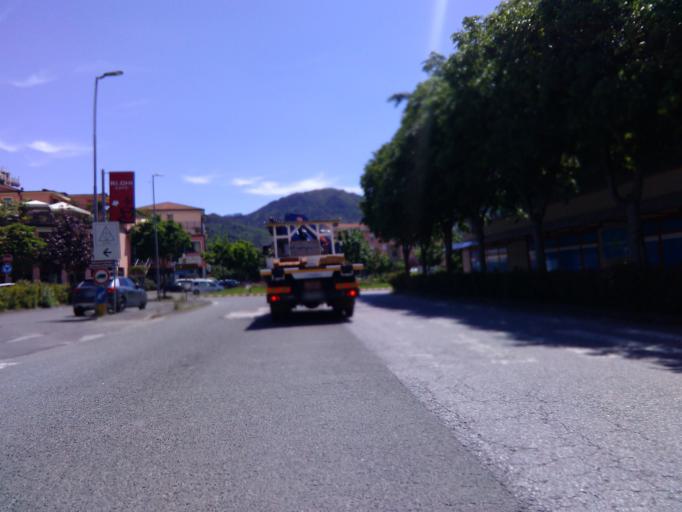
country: IT
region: Tuscany
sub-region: Provincia di Massa-Carrara
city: Aulla
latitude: 44.2156
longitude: 9.9667
